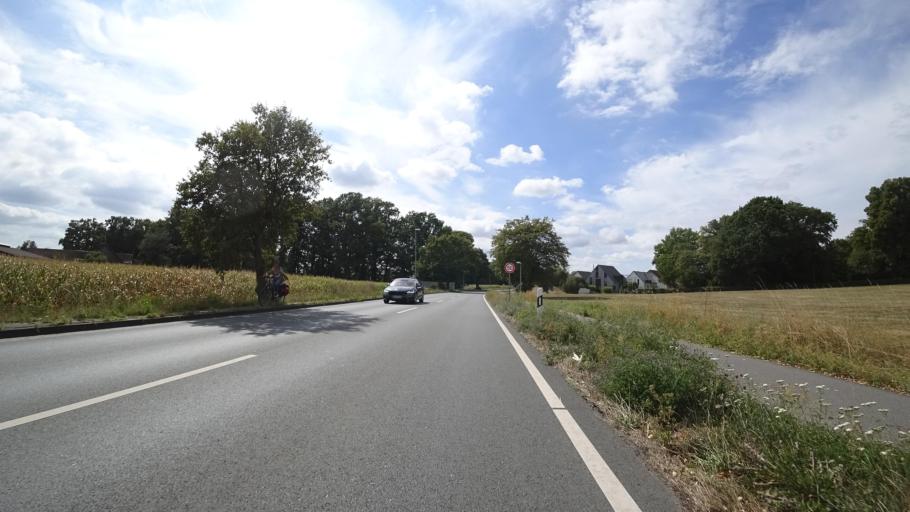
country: DE
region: North Rhine-Westphalia
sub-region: Regierungsbezirk Detmold
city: Guetersloh
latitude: 51.9152
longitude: 8.4404
